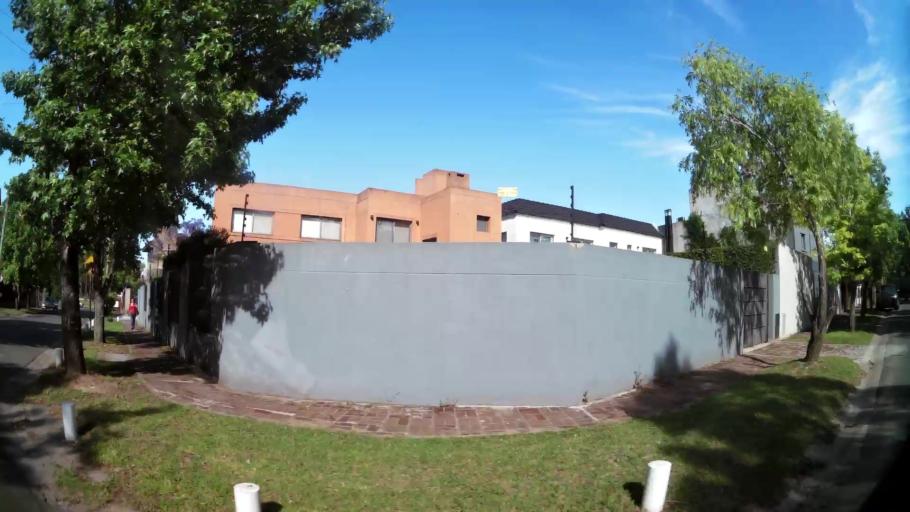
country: AR
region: Buenos Aires
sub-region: Partido de Tigre
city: Tigre
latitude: -34.4844
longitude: -58.5801
